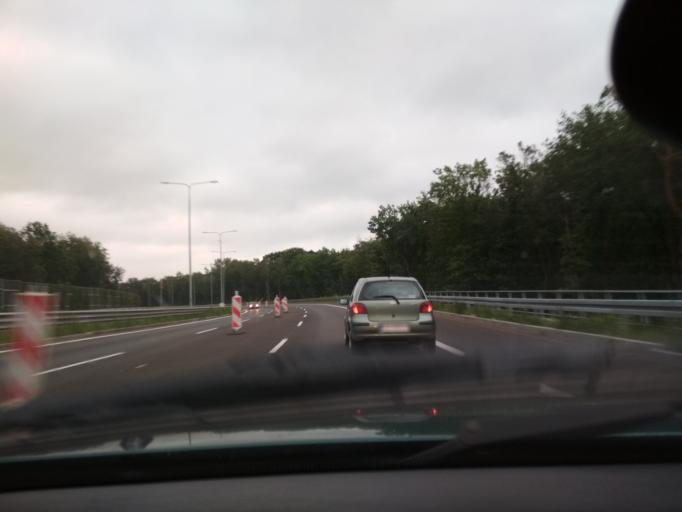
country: PL
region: Silesian Voivodeship
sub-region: Powiat gliwicki
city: Przyszowice
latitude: 50.2856
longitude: 18.7644
